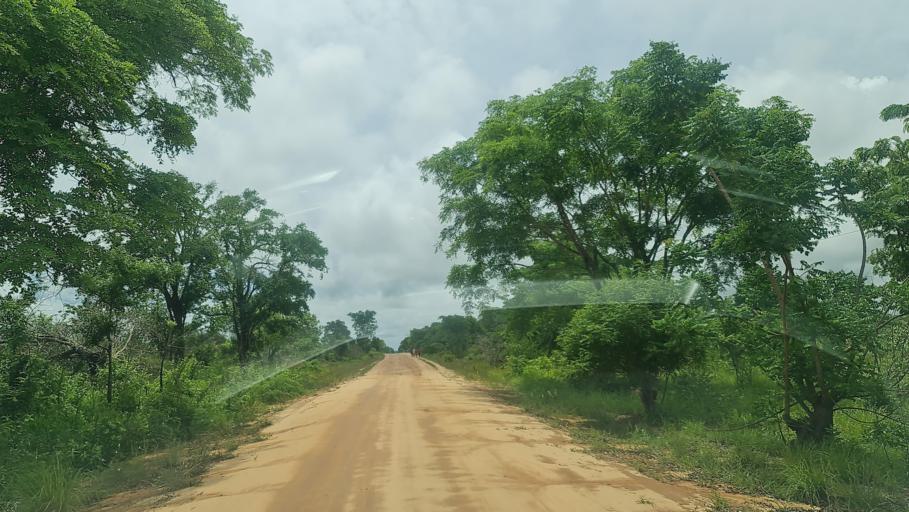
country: MZ
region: Zambezia
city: Quelimane
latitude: -17.2557
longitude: 37.2256
